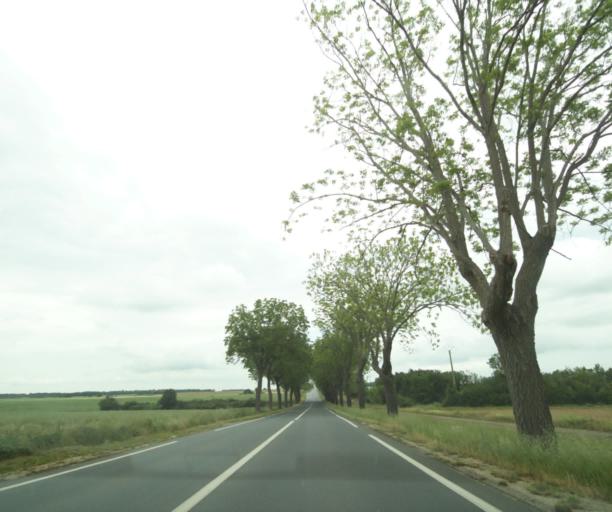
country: FR
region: Poitou-Charentes
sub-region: Departement des Deux-Sevres
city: Saint-Jean-de-Thouars
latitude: 46.9284
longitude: -0.1990
